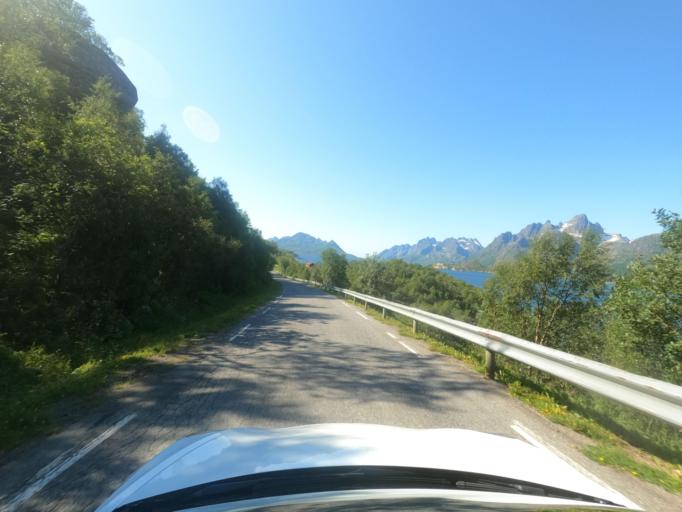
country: NO
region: Nordland
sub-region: Hadsel
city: Stokmarknes
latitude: 68.3488
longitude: 15.0588
